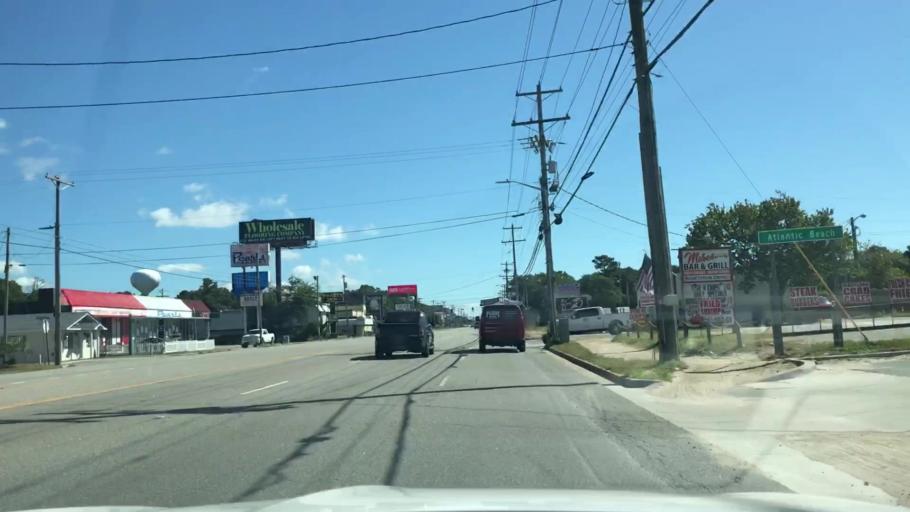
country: US
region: South Carolina
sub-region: Horry County
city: North Myrtle Beach
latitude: 33.8047
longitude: -78.7211
